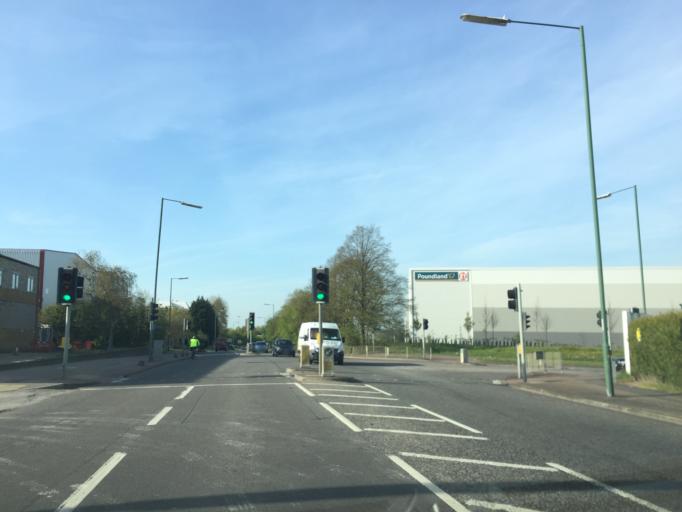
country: GB
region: England
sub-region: Essex
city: Roydon
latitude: 51.7672
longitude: 0.0679
